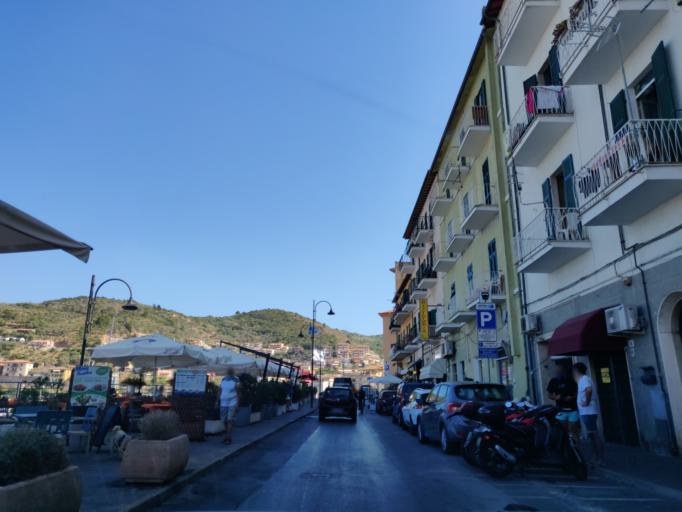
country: IT
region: Tuscany
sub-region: Provincia di Grosseto
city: Monte Argentario
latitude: 42.4368
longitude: 11.1199
